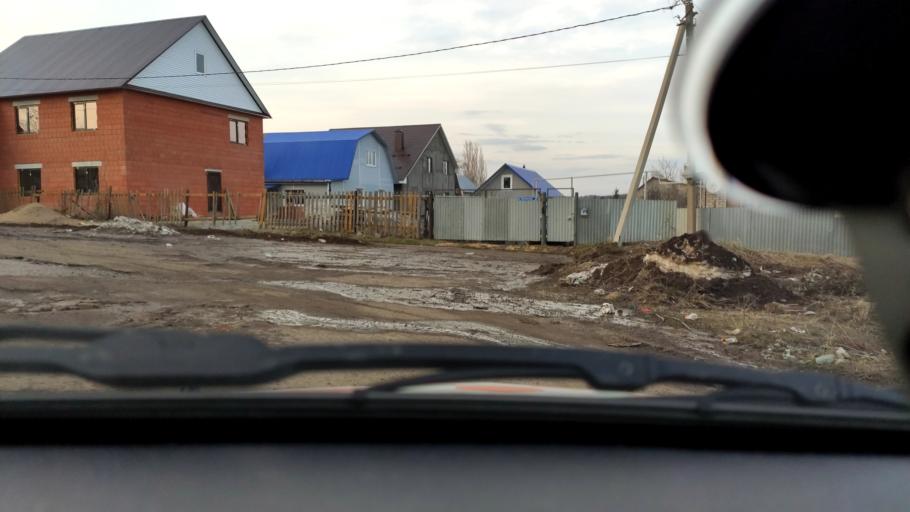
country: RU
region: Bashkortostan
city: Ufa
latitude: 54.8344
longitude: 56.1526
